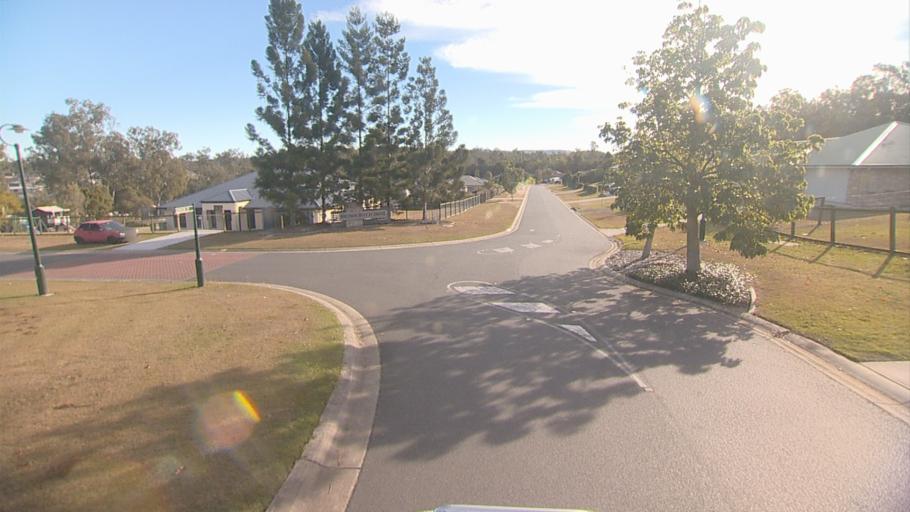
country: AU
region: Queensland
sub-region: Logan
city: North Maclean
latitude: -27.7962
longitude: 152.9567
